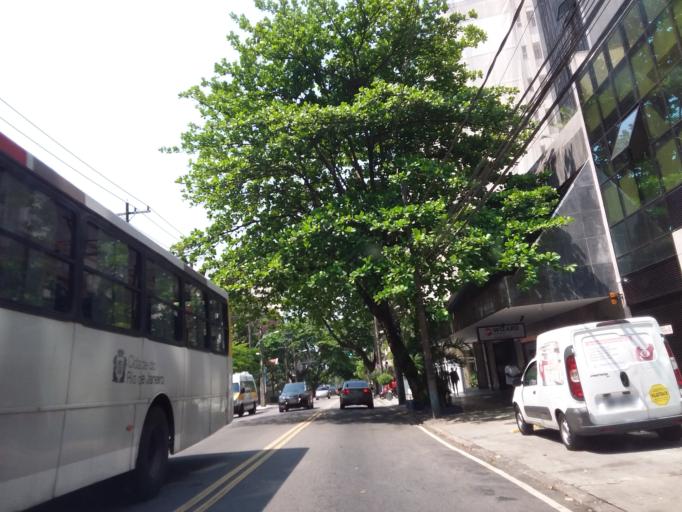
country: BR
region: Rio de Janeiro
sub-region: Rio De Janeiro
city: Rio de Janeiro
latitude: -22.9769
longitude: -43.2299
